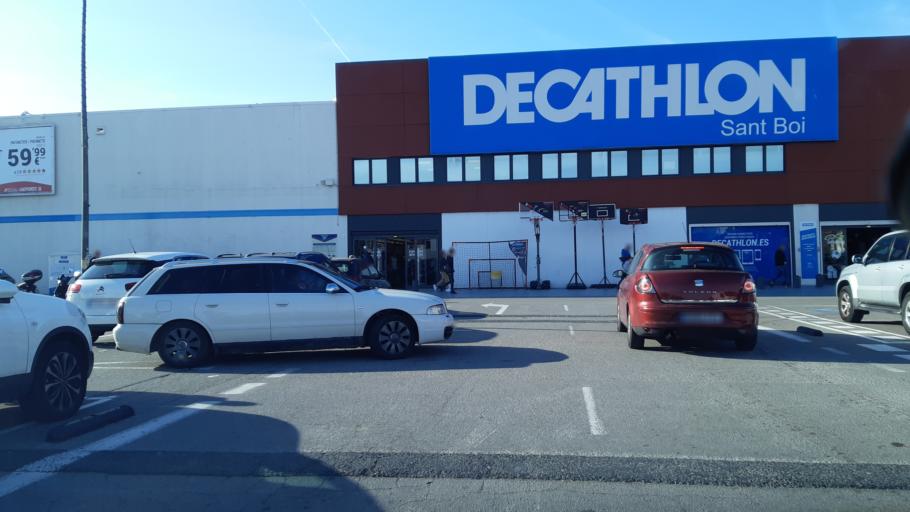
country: ES
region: Catalonia
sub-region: Provincia de Barcelona
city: Sant Boi de Llobregat
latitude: 41.3279
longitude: 2.0482
